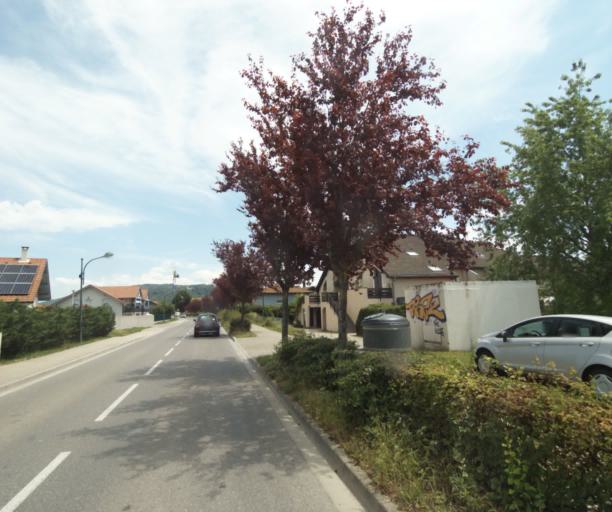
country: FR
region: Rhone-Alpes
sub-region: Departement de la Haute-Savoie
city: Douvaine
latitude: 46.3070
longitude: 6.2946
